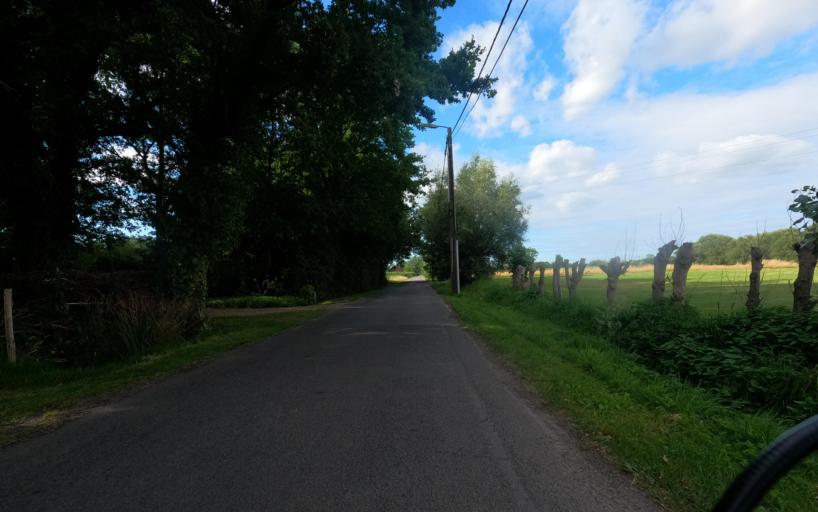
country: BE
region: Flanders
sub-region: Provincie Antwerpen
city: Heist-op-den-Berg
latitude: 51.0324
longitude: 4.7253
